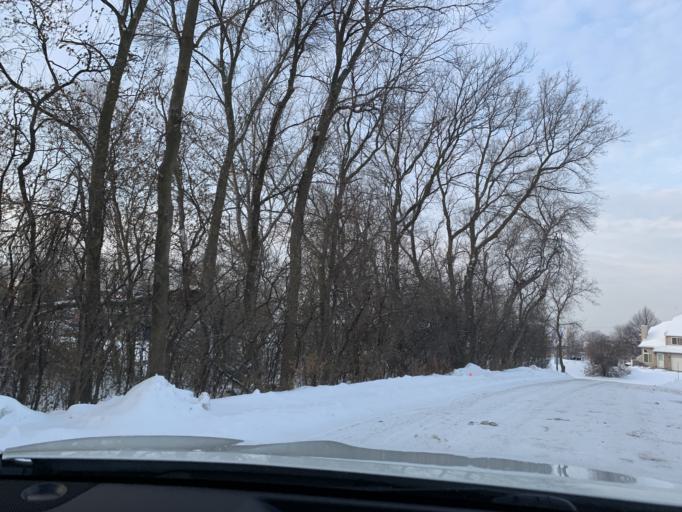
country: US
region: Minnesota
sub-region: Anoka County
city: Coon Rapids
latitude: 45.1635
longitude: -93.2882
